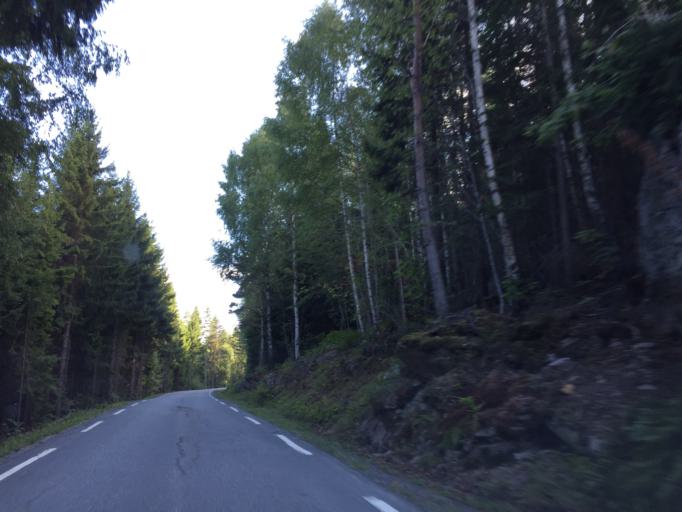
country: NO
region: Buskerud
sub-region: Ovre Eiker
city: Hokksund
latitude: 59.6504
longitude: 9.9174
